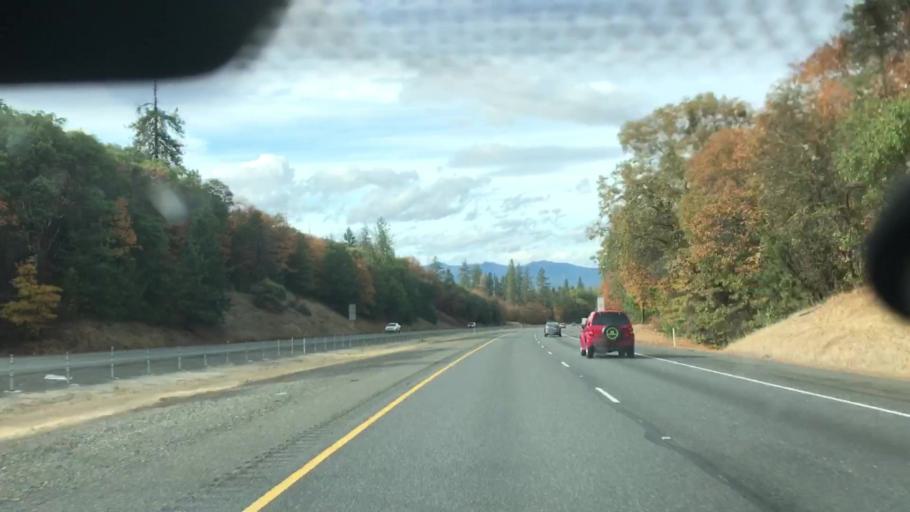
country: US
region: Oregon
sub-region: Josephine County
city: Grants Pass
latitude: 42.4818
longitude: -123.3573
